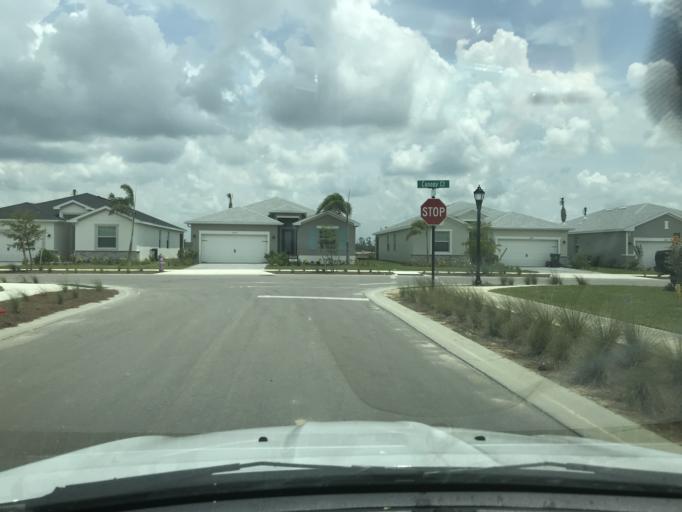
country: US
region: Florida
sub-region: Lee County
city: Olga
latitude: 26.7758
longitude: -81.7395
